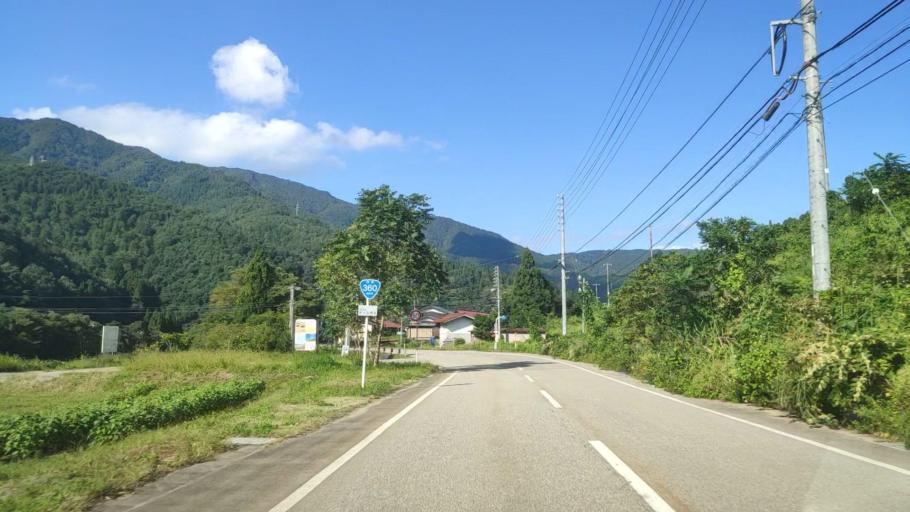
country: JP
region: Gifu
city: Takayama
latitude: 36.3241
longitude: 137.1361
